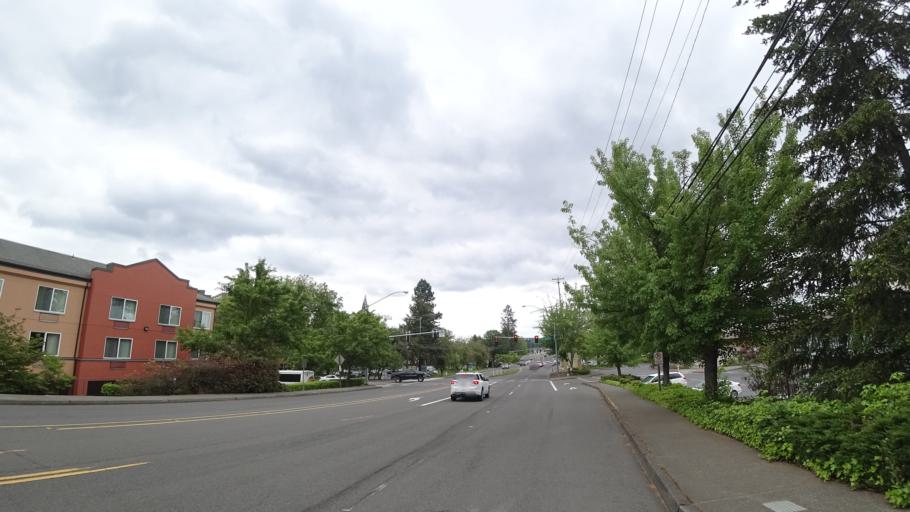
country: US
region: Oregon
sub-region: Washington County
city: Tigard
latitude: 45.4475
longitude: -122.7759
